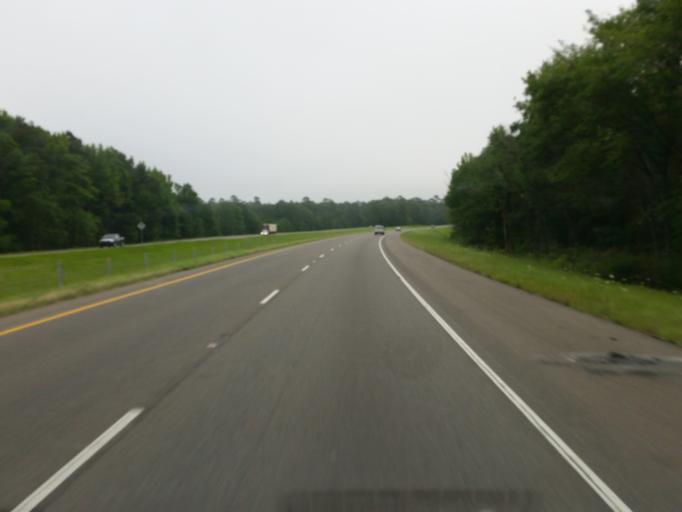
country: US
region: Louisiana
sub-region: Bossier Parish
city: Haughton
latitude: 32.5724
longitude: -93.4841
